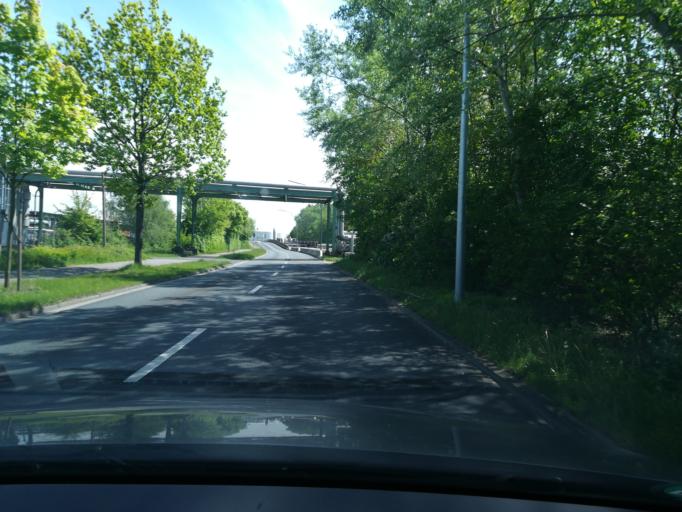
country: DE
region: Hamburg
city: Altona
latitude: 53.5015
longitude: 9.9467
